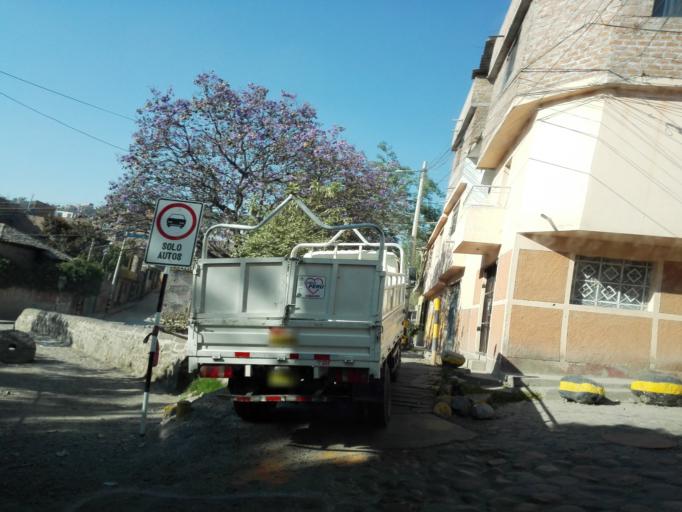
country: PE
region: Ayacucho
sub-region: Provincia de Huamanga
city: Ayacucho
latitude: -13.1627
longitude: -74.2211
